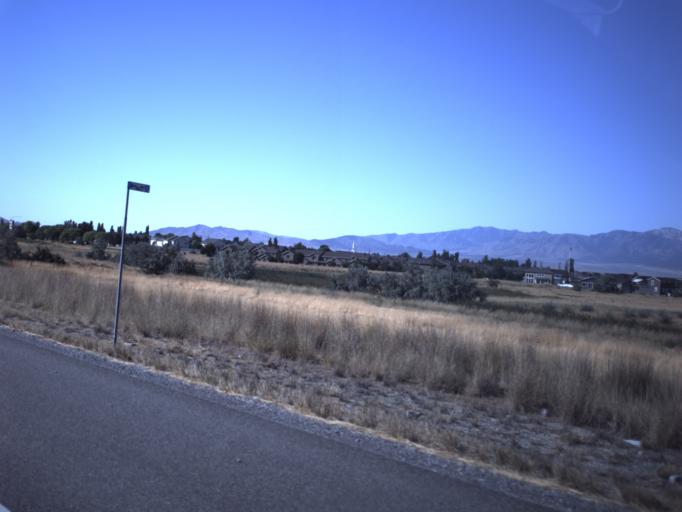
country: US
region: Utah
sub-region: Tooele County
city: Stansbury park
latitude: 40.6574
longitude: -112.2898
